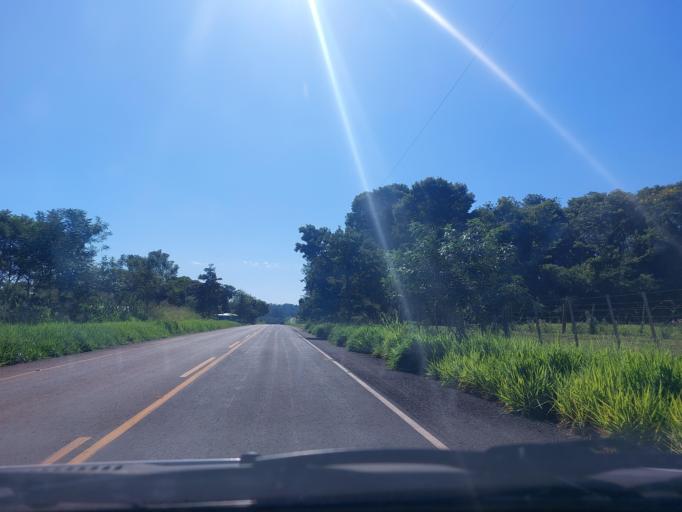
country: PY
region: San Pedro
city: Guayaybi
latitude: -24.3017
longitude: -56.1451
